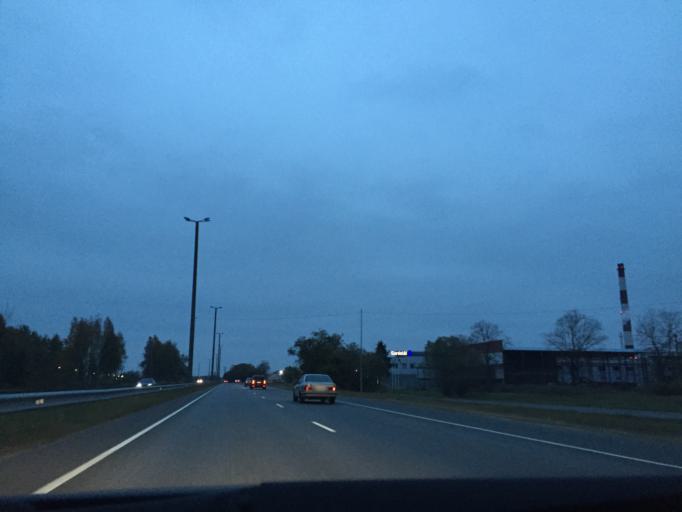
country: LV
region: Marupe
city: Marupe
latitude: 56.8838
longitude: 24.0735
